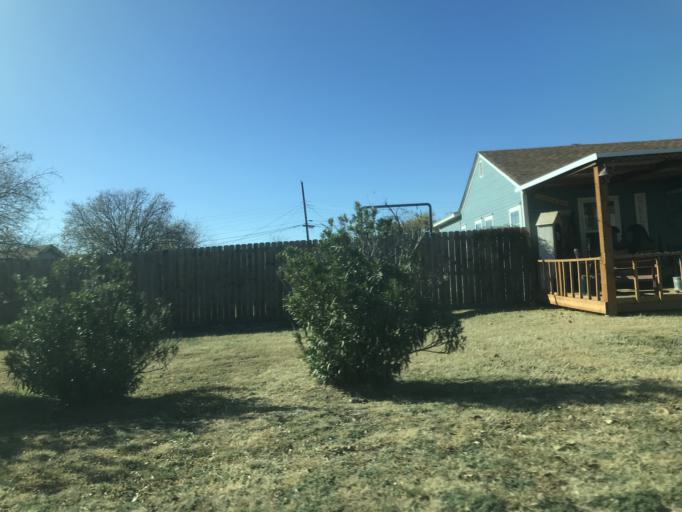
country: US
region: Texas
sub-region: Taylor County
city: Abilene
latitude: 32.4334
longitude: -99.7560
